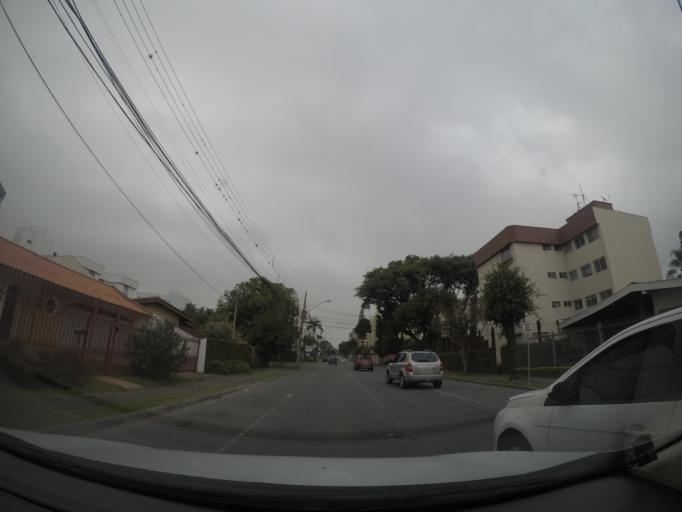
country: BR
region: Parana
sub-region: Curitiba
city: Curitiba
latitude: -25.4008
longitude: -49.2594
